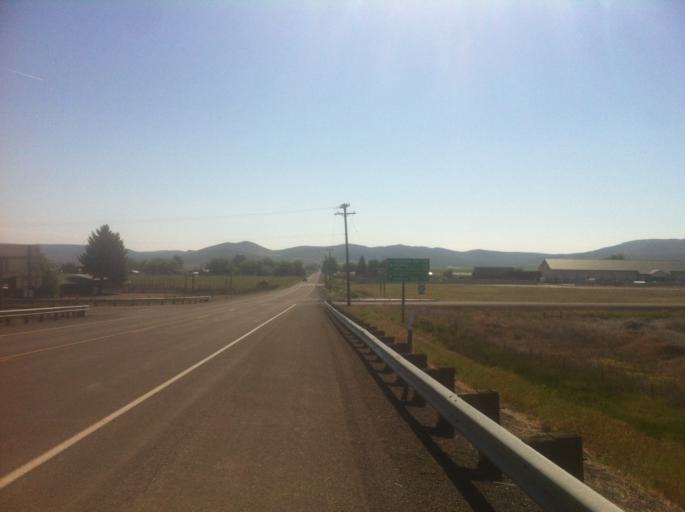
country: US
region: Oregon
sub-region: Baker County
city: Baker City
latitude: 44.8033
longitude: -117.8109
